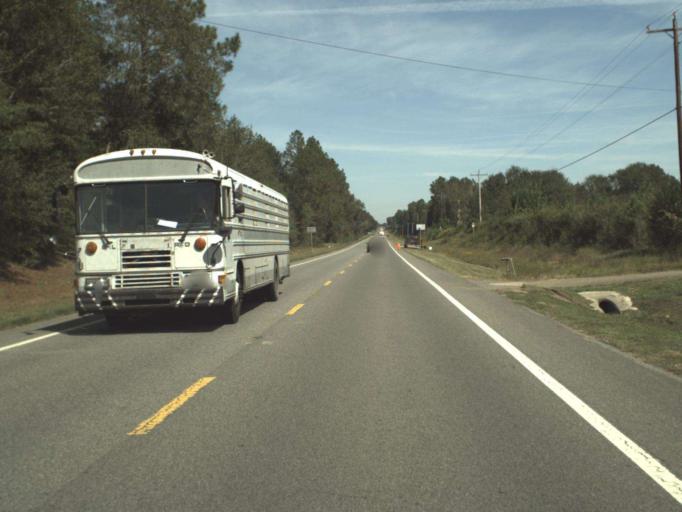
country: US
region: Florida
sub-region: Washington County
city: Chipley
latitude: 30.6898
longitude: -85.5666
